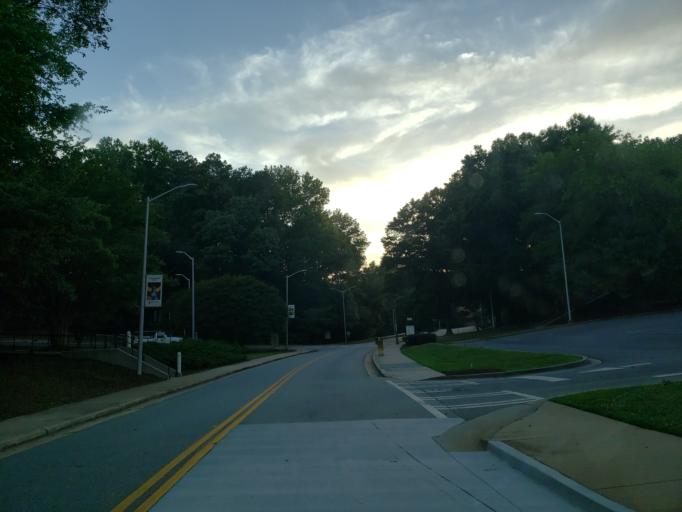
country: US
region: Georgia
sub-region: Cobb County
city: Kennesaw
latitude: 34.0366
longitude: -84.5839
